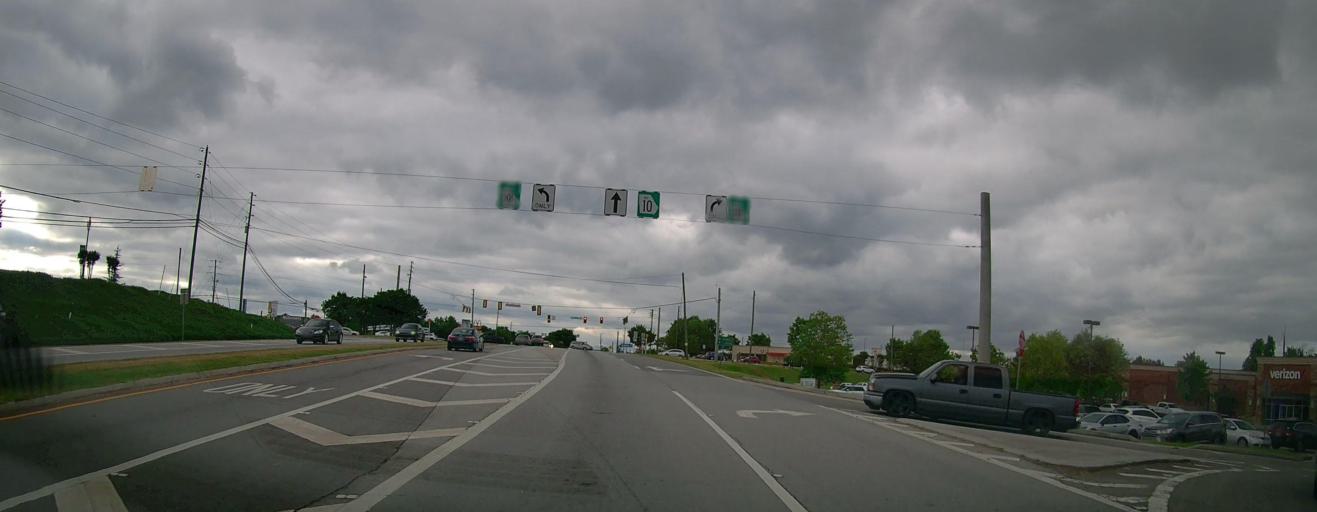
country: US
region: Georgia
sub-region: Walton County
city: Monroe
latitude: 33.7941
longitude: -83.7415
